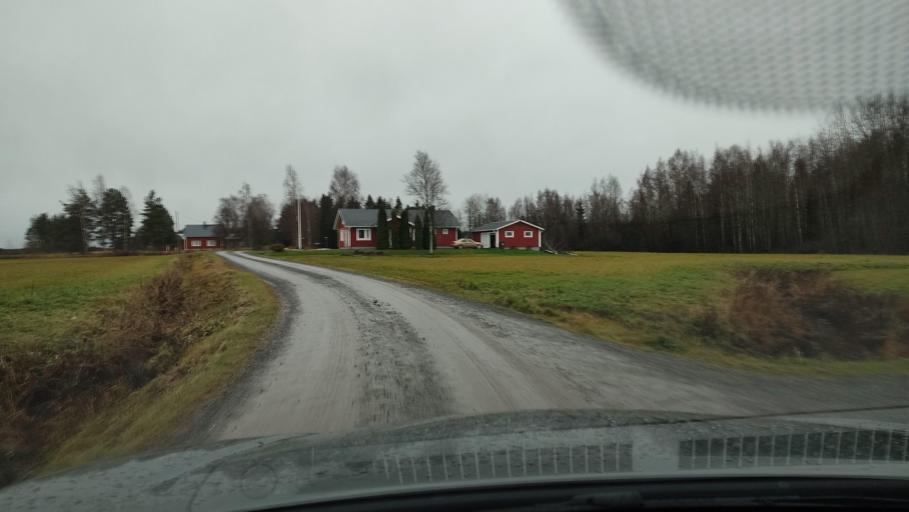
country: FI
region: Southern Ostrobothnia
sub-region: Suupohja
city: Karijoki
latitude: 62.2383
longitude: 21.5501
